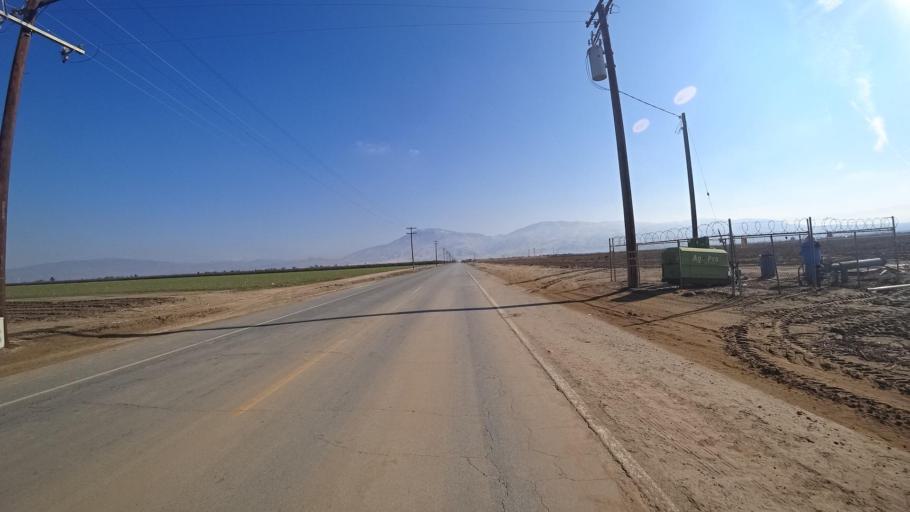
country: US
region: California
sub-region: Kern County
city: Arvin
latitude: 35.1943
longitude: -118.8557
